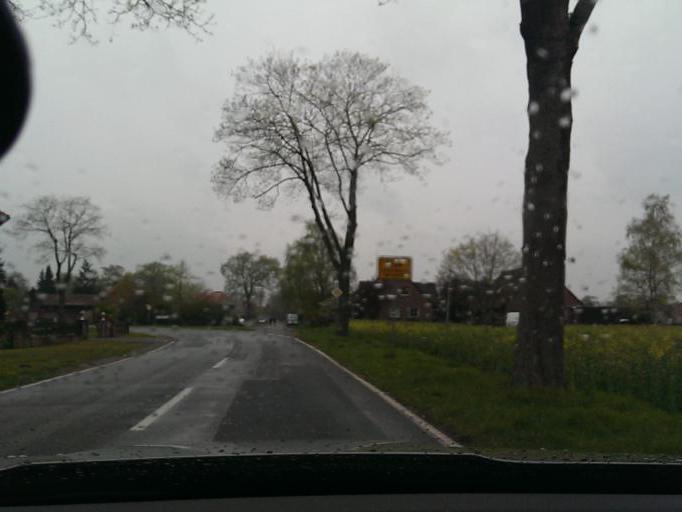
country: DE
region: Lower Saxony
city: Elze
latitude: 52.5857
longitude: 9.7443
